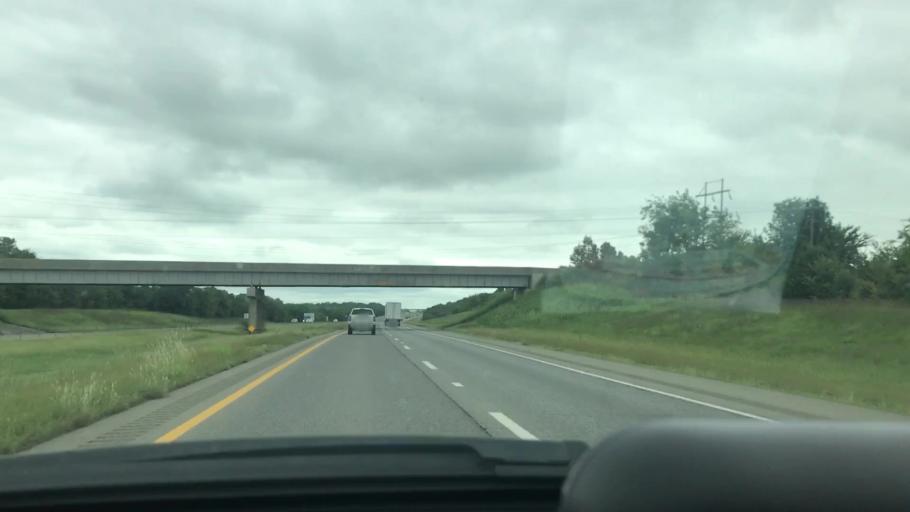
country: US
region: Oklahoma
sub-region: McIntosh County
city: Checotah
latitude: 35.3905
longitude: -95.5658
